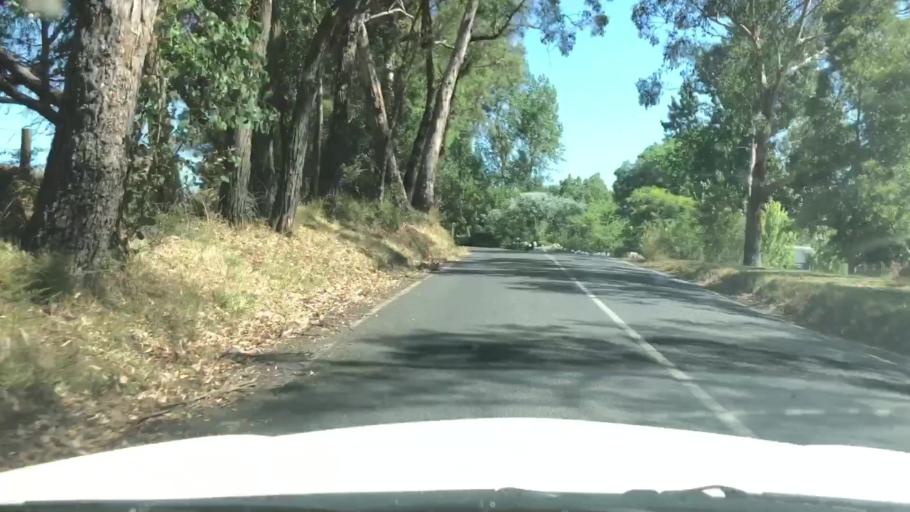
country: AU
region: Victoria
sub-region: Yarra Ranges
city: Macclesfield
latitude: -37.8647
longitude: 145.4790
